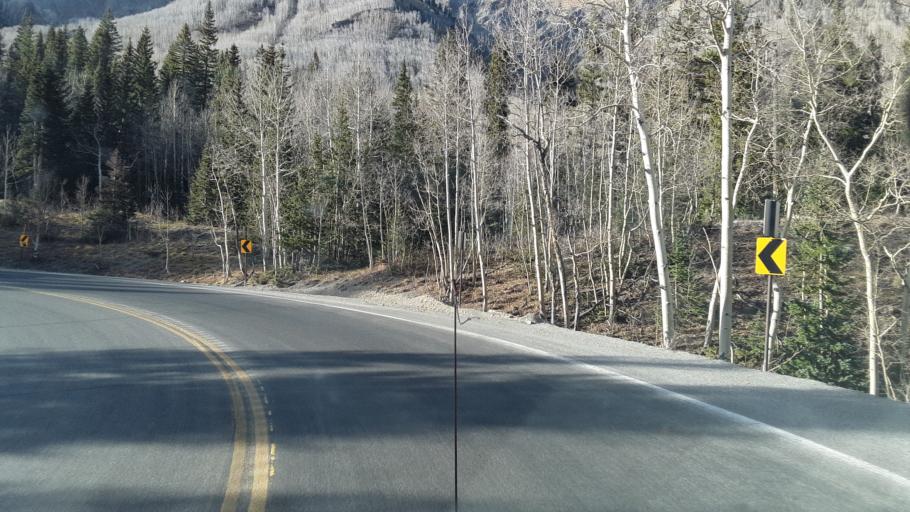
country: US
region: Colorado
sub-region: Ouray County
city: Ouray
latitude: 37.9251
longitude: -107.6943
